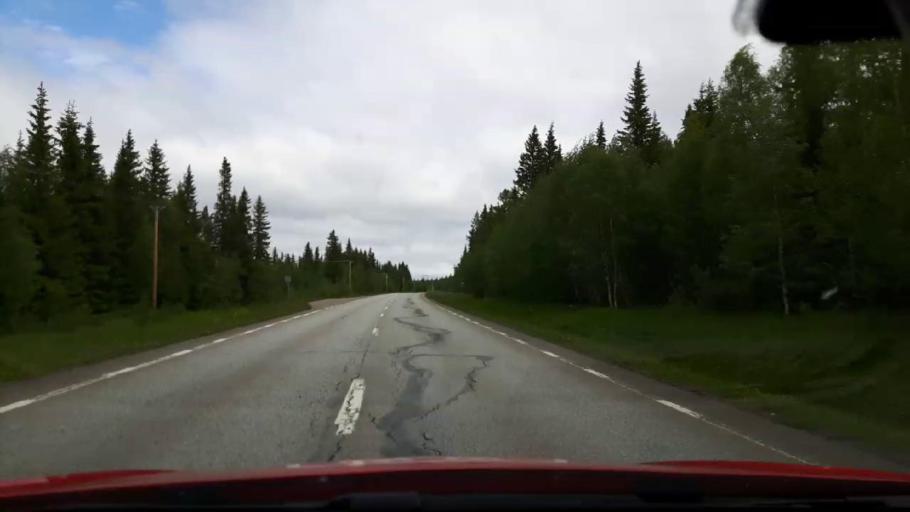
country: SE
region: Jaemtland
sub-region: Krokoms Kommun
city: Krokom
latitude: 63.4672
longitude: 14.4962
